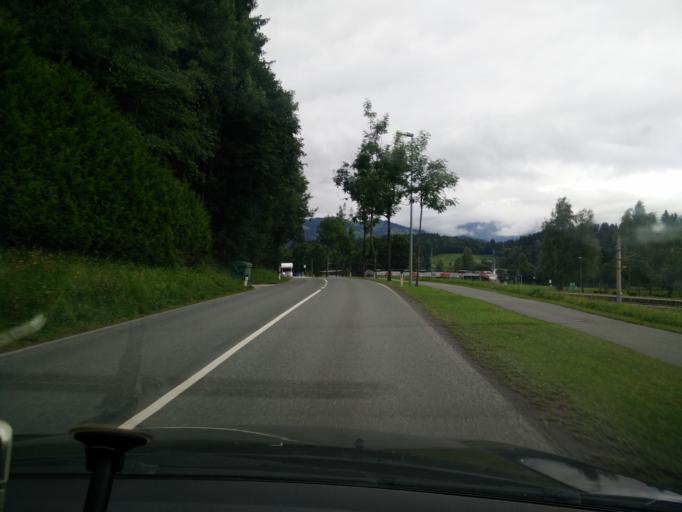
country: AT
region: Tyrol
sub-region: Politischer Bezirk Kitzbuhel
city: Kitzbuhel
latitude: 47.4522
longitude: 12.3716
